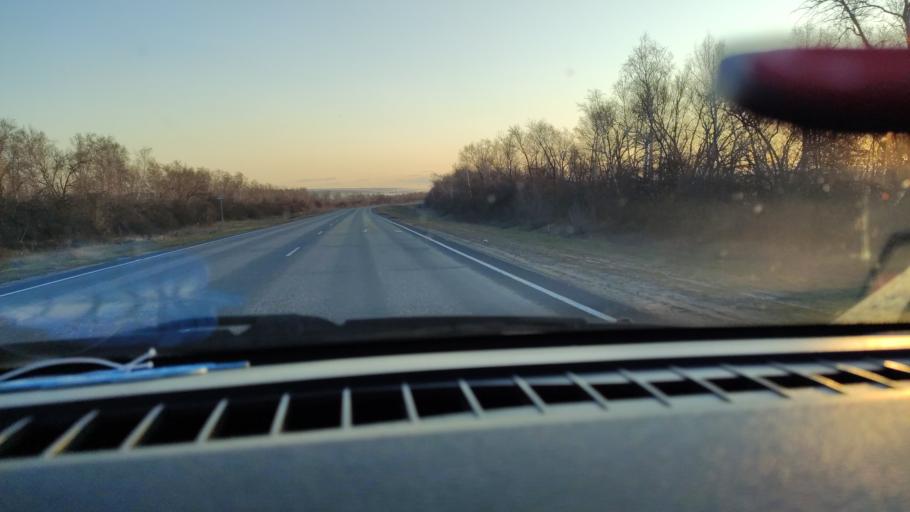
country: RU
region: Saratov
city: Sinodskoye
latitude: 51.9525
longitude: 46.6104
